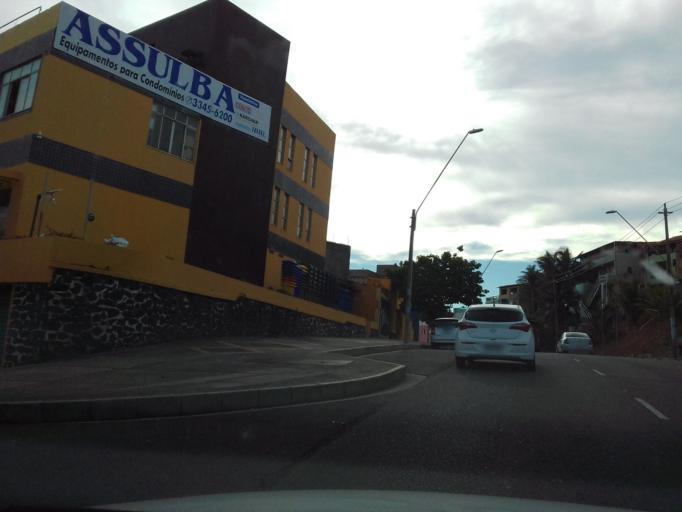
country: BR
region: Bahia
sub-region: Salvador
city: Salvador
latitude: -13.0120
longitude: -38.4729
